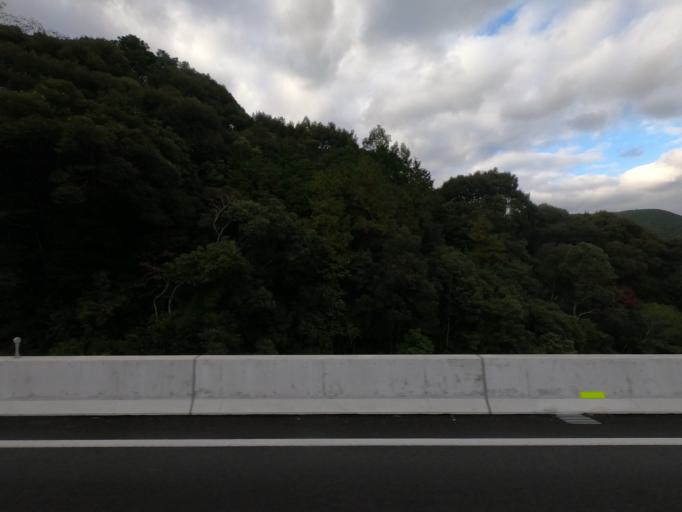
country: JP
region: Kumamoto
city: Minamata
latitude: 32.2297
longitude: 130.4484
